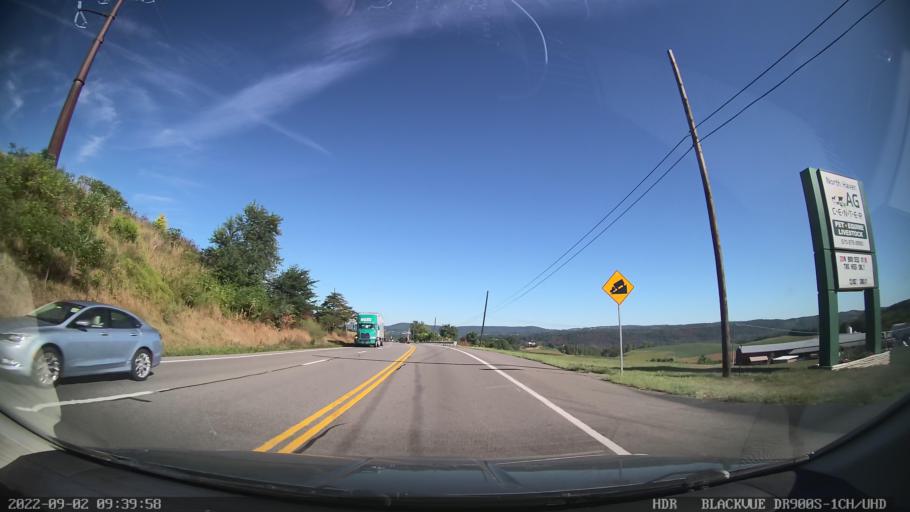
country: US
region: Pennsylvania
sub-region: Montour County
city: Mechanicsville
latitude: 40.9196
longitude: -76.5860
